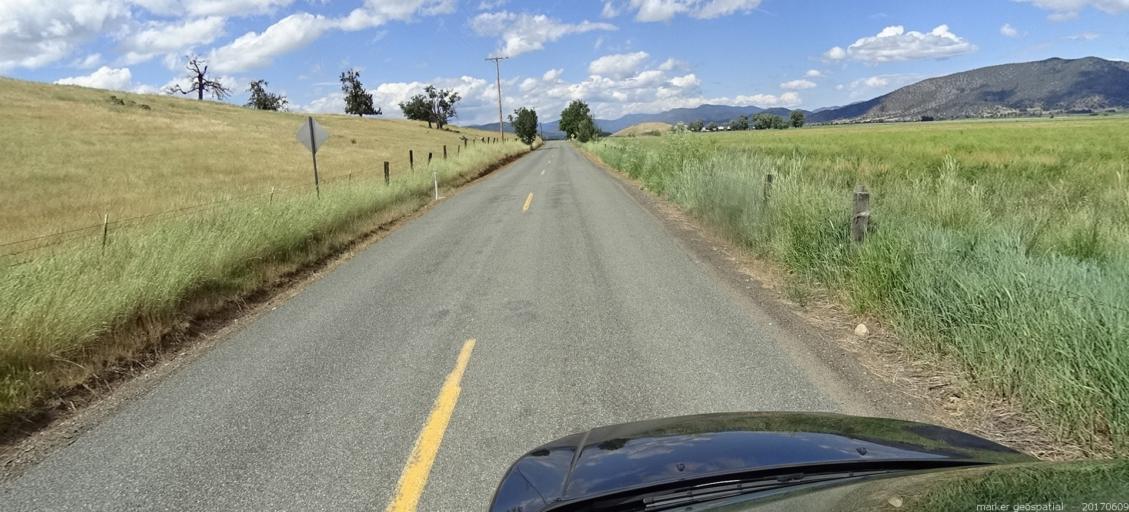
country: US
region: California
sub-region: Siskiyou County
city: Yreka
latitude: 41.4818
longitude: -122.8769
